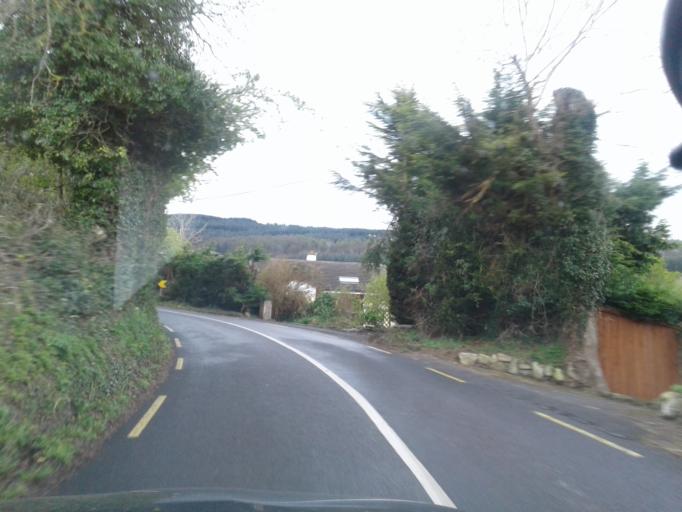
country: IE
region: Leinster
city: Ballyboden
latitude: 53.2518
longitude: -6.3025
